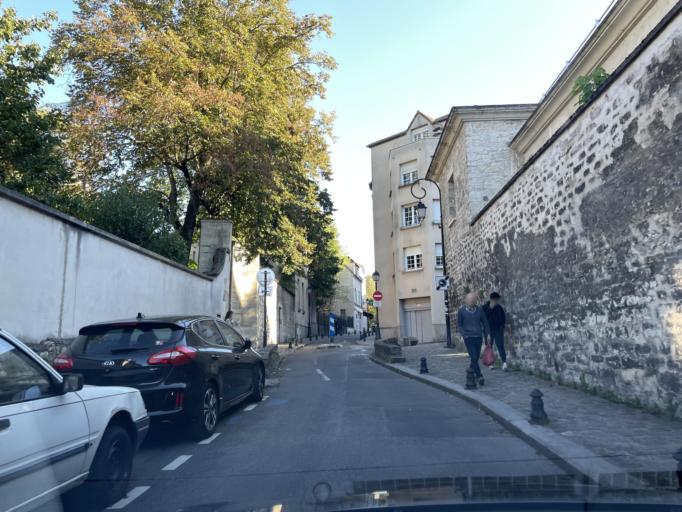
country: FR
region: Ile-de-France
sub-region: Departement du Val-de-Marne
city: Joinville-le-Pont
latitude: 48.8134
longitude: 2.4720
